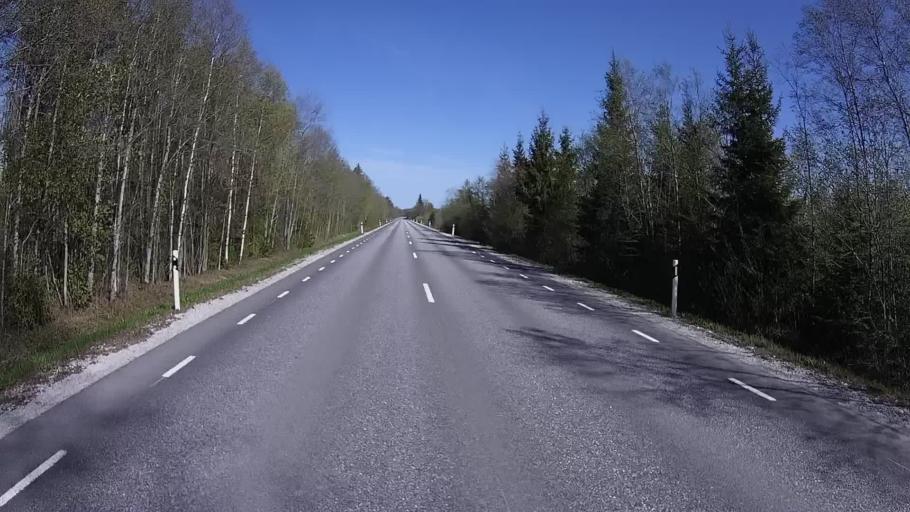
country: EE
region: Raplamaa
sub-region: Jaervakandi vald
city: Jarvakandi
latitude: 58.8663
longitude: 24.7854
